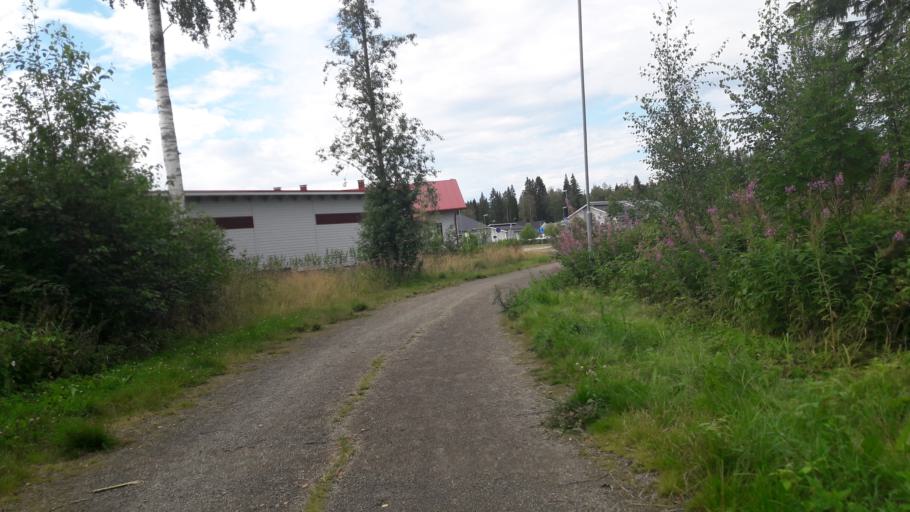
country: FI
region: North Karelia
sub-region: Joensuu
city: Joensuu
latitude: 62.5716
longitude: 29.8259
